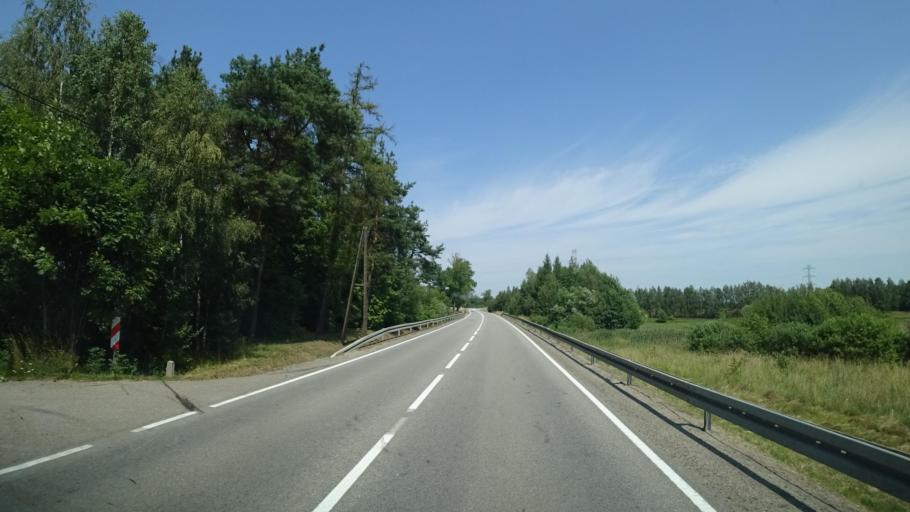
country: PL
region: Pomeranian Voivodeship
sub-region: Powiat koscierski
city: Koscierzyna
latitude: 54.1516
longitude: 18.0299
